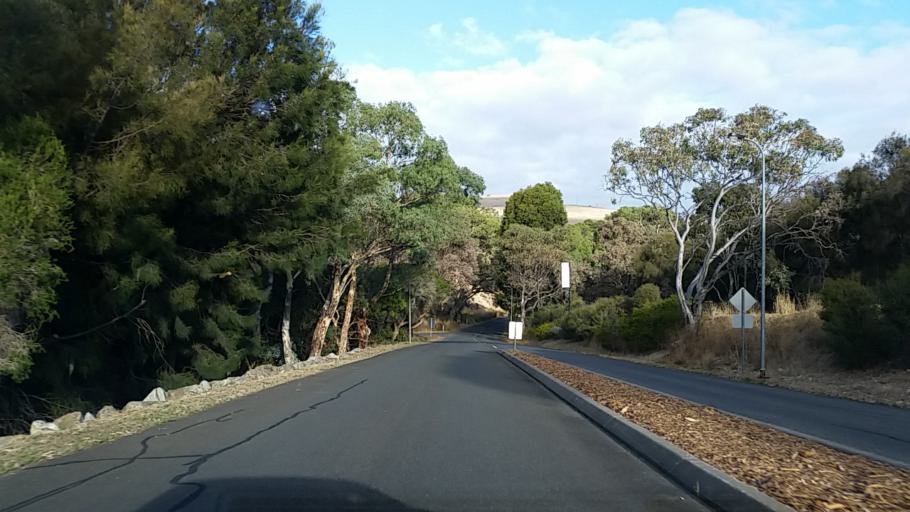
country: AU
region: South Australia
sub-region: Yankalilla
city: Normanville
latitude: -35.5060
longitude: 138.2604
